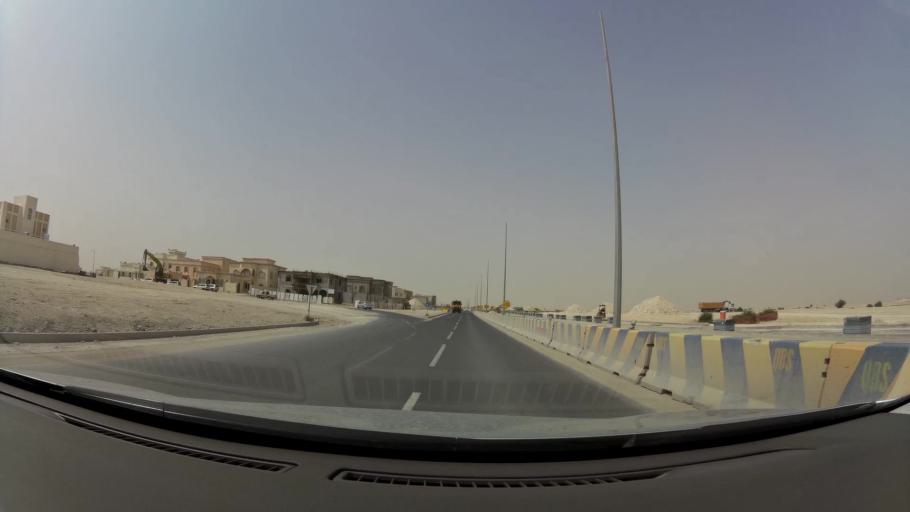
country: QA
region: Baladiyat ar Rayyan
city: Ar Rayyan
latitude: 25.2607
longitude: 51.3756
